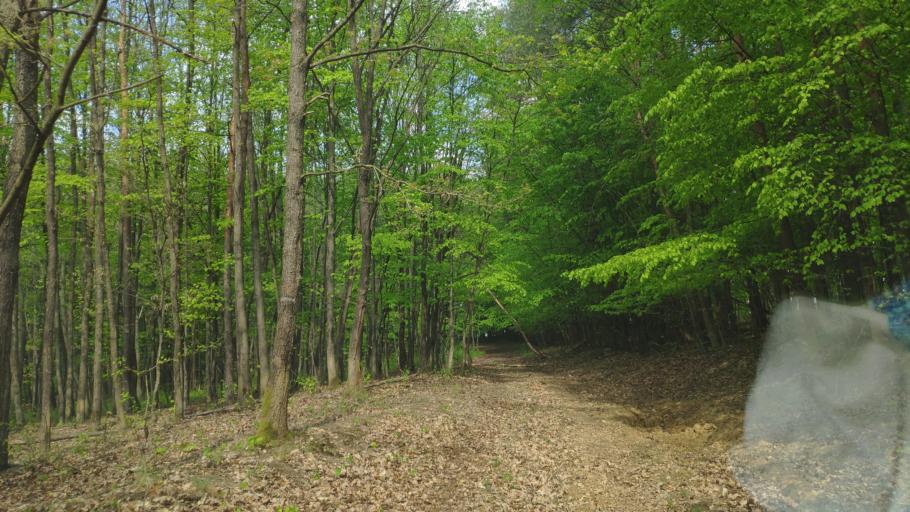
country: SK
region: Kosicky
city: Moldava nad Bodvou
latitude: 48.5398
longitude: 20.9429
